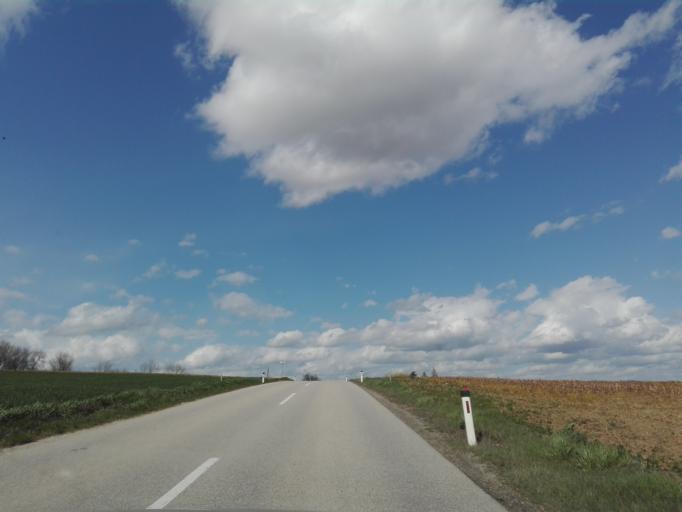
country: AT
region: Upper Austria
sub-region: Wels-Land
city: Holzhausen
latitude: 48.2598
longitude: 14.1123
